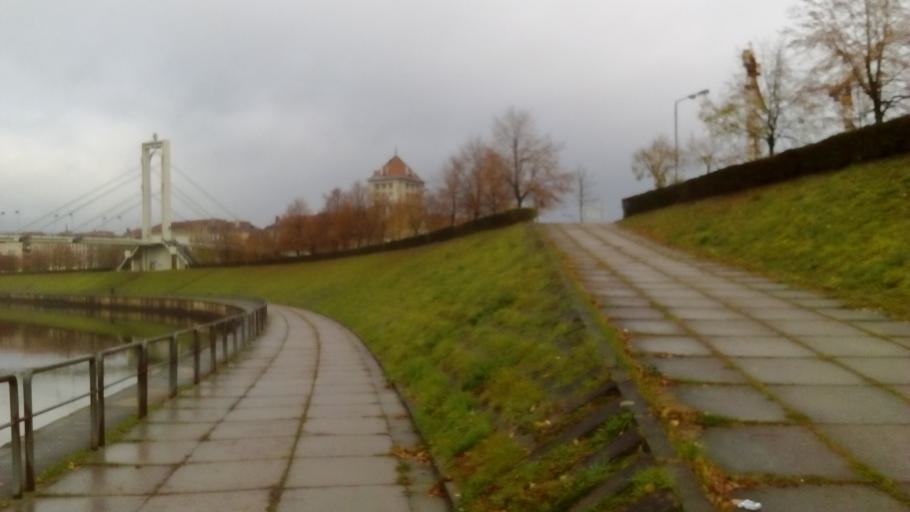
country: LT
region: Kauno apskritis
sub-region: Kaunas
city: Kaunas
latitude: 54.8925
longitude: 23.9156
